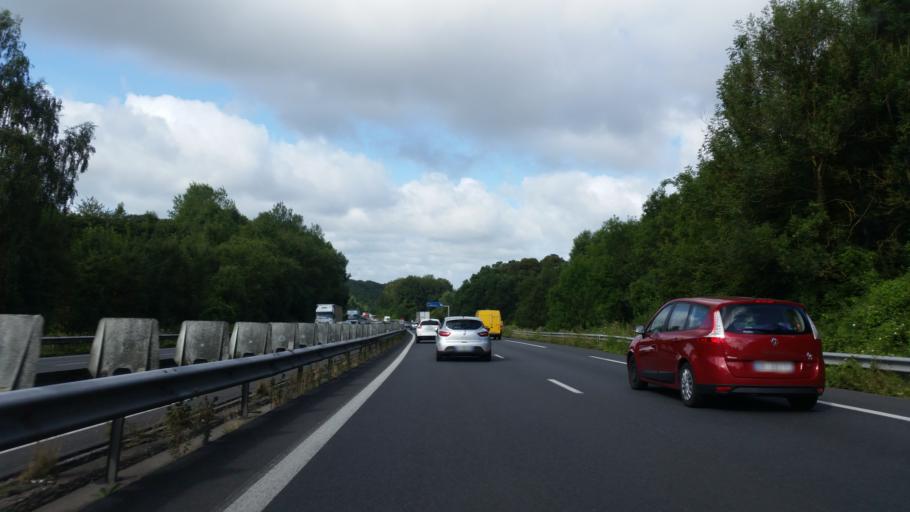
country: FR
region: Lower Normandy
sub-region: Departement du Calvados
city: Blonville-sur-Mer
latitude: 49.2491
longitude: 0.0617
